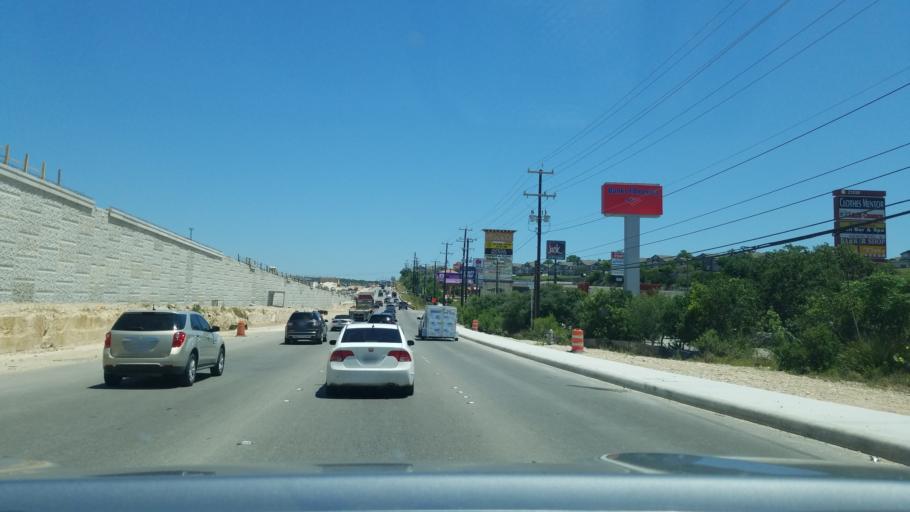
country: US
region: Texas
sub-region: Bexar County
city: Hollywood Park
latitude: 29.6380
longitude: -98.4554
